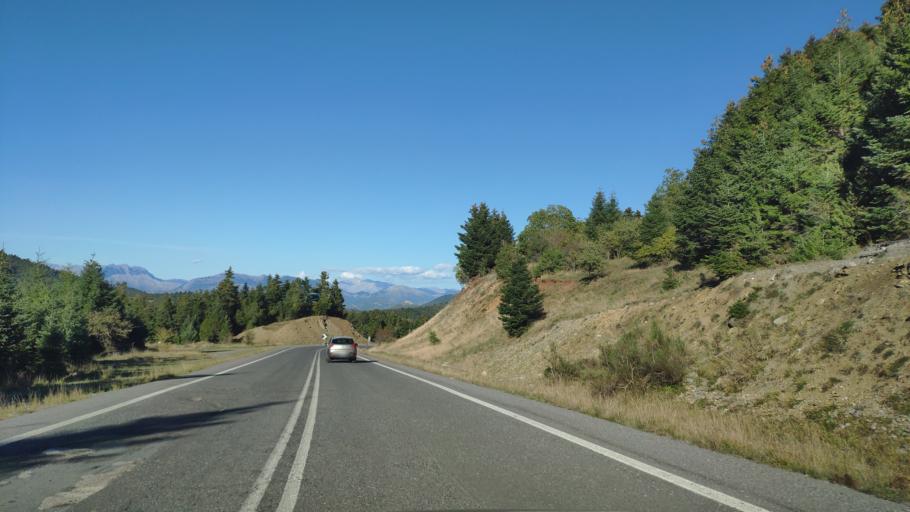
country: GR
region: Peloponnese
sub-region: Nomos Arkadias
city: Langadhia
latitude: 37.6567
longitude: 22.1378
